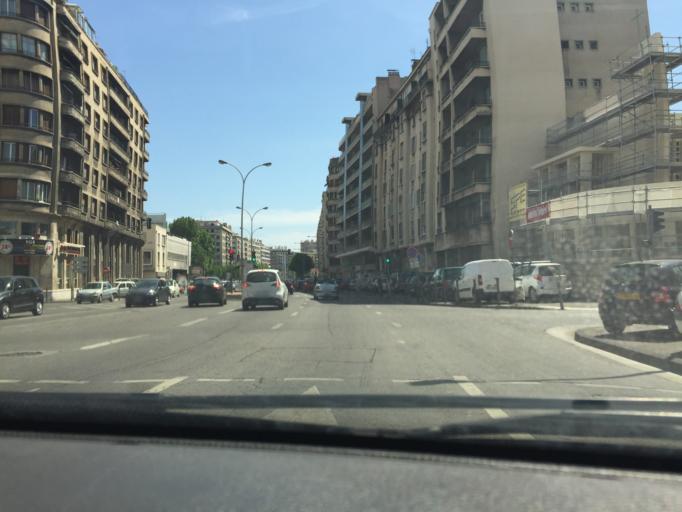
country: FR
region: Provence-Alpes-Cote d'Azur
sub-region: Departement des Bouches-du-Rhone
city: Marseille 04
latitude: 43.3021
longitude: 5.4005
